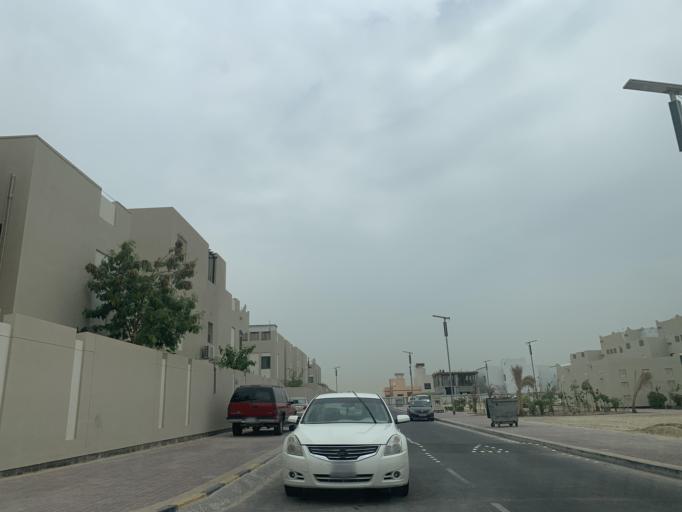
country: BH
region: Northern
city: Madinat `Isa
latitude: 26.1782
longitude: 50.5154
